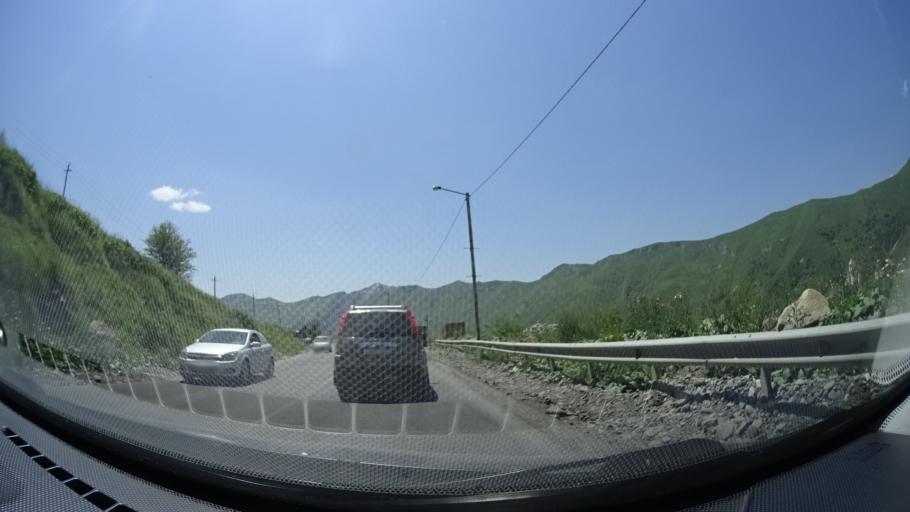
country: GE
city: Gudauri
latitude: 42.4611
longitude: 44.4824
